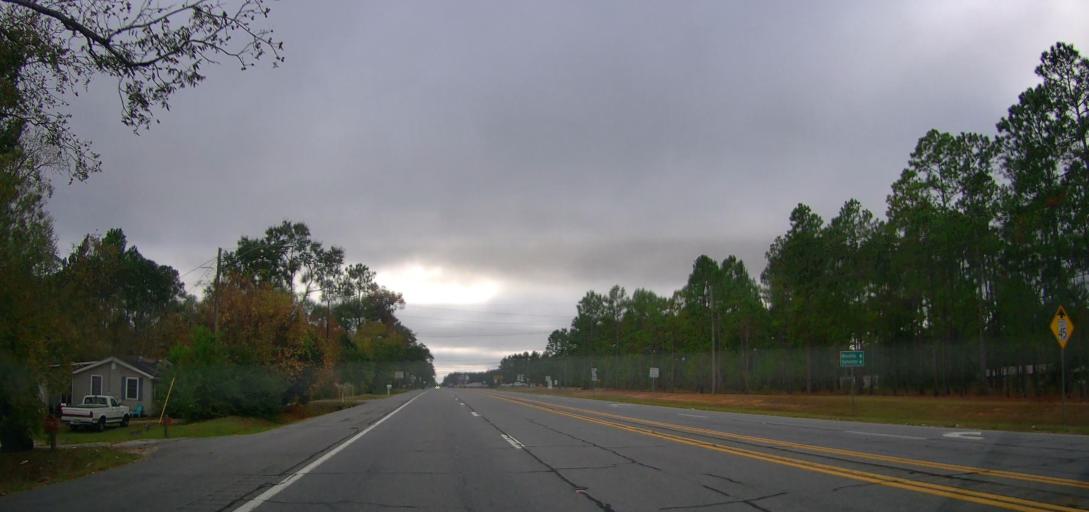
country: US
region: Georgia
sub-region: Tift County
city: Omega
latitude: 31.2811
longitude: -83.6819
